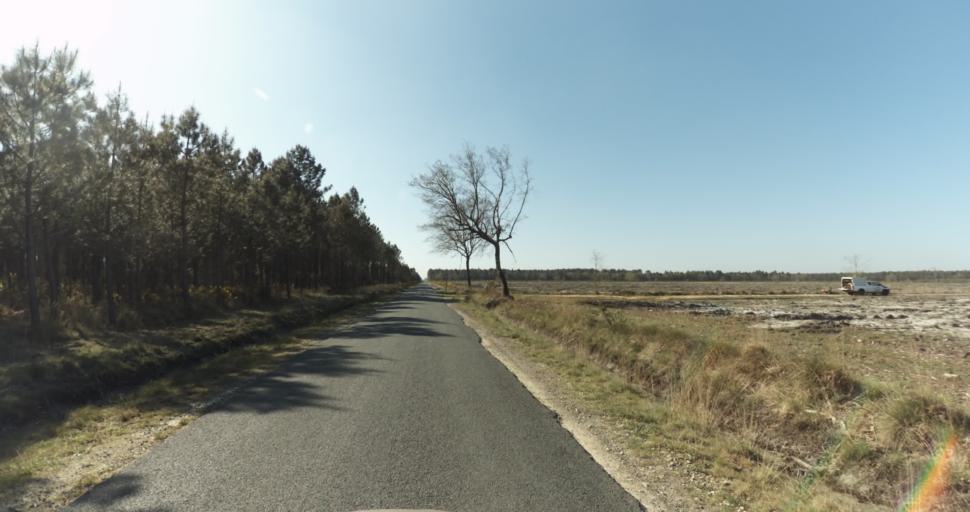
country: FR
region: Aquitaine
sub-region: Departement de la Gironde
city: Martignas-sur-Jalle
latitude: 44.7920
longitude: -0.8646
